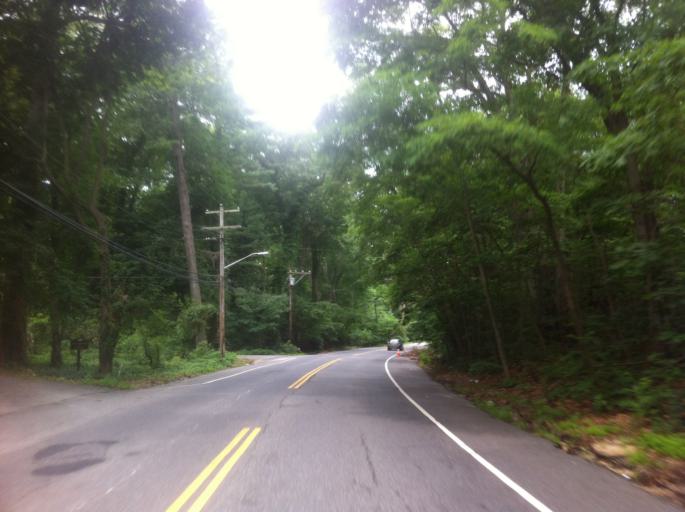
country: US
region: New York
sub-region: Nassau County
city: Oyster Bay Cove
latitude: 40.8570
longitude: -73.5150
